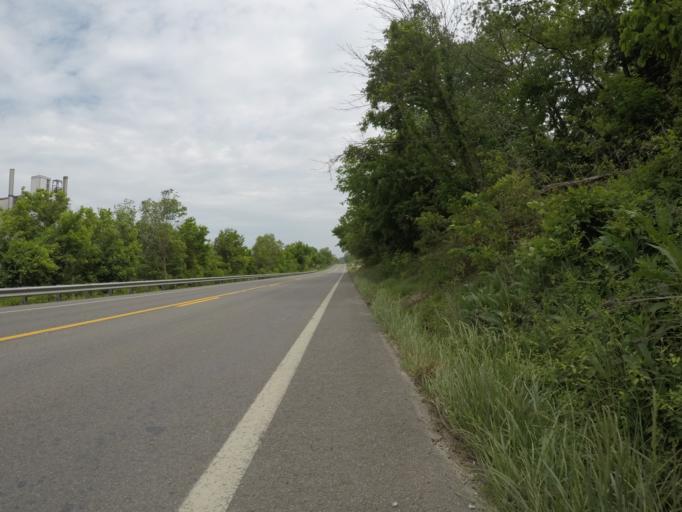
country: US
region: West Virginia
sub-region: Wayne County
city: Kenova
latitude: 38.3552
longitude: -82.5932
